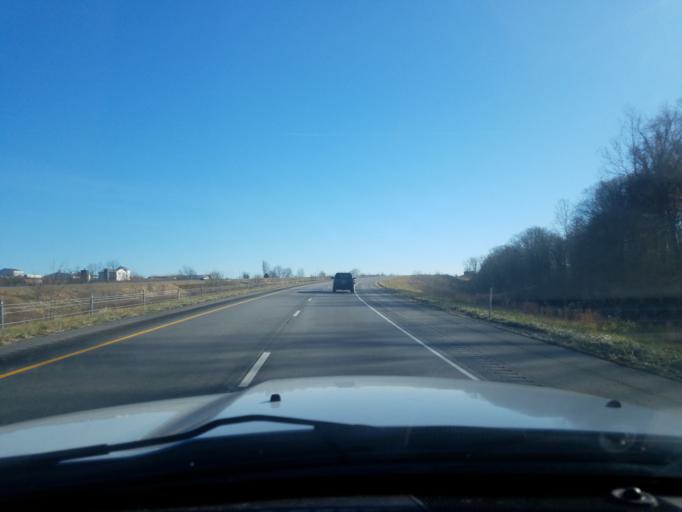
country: US
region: Indiana
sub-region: Dubois County
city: Ferdinand
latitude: 38.2330
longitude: -86.6722
